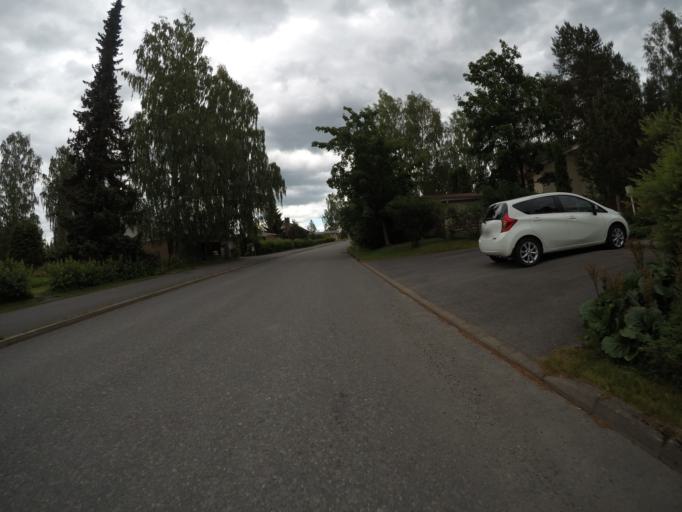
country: FI
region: Haeme
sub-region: Haemeenlinna
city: Haemeenlinna
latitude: 60.9863
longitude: 24.4338
